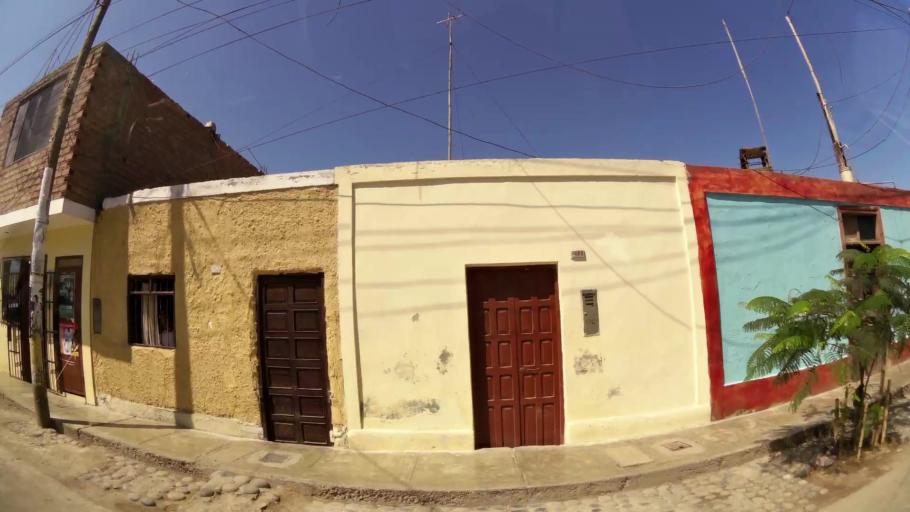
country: PE
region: Lima
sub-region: Provincia de Canete
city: San Vicente de Canete
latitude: -13.0282
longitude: -76.4808
